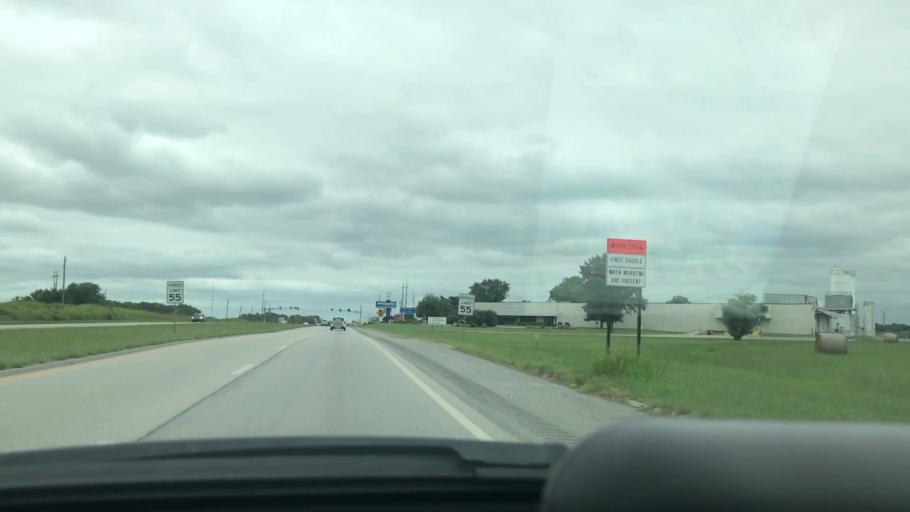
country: US
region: Oklahoma
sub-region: Mayes County
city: Chouteau
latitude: 36.2444
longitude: -95.3367
